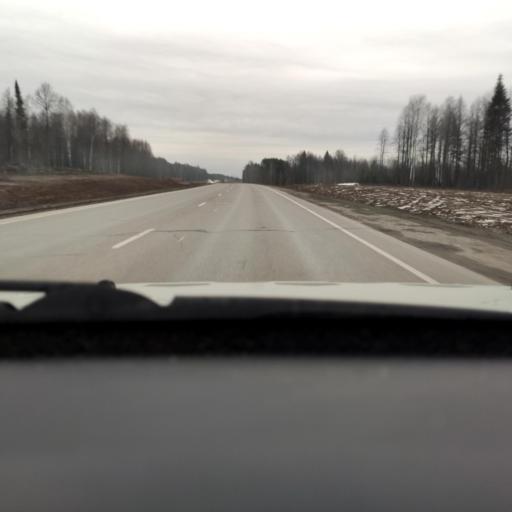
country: RU
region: Perm
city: Polazna
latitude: 58.1292
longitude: 56.4215
